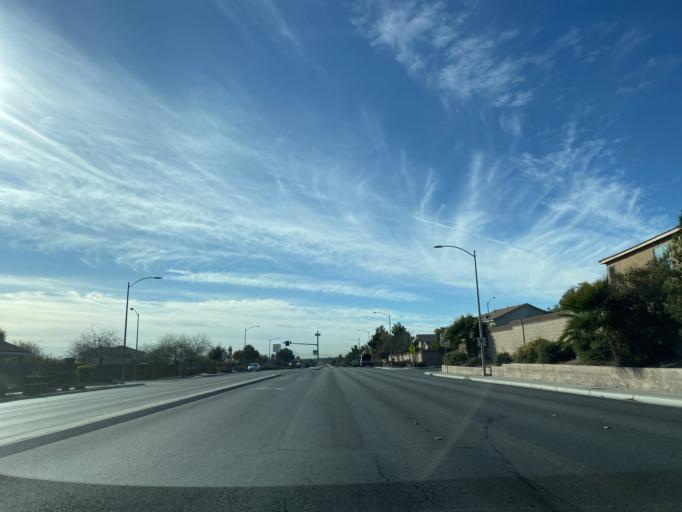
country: US
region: Nevada
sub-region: Clark County
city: North Las Vegas
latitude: 36.2659
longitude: -115.2071
